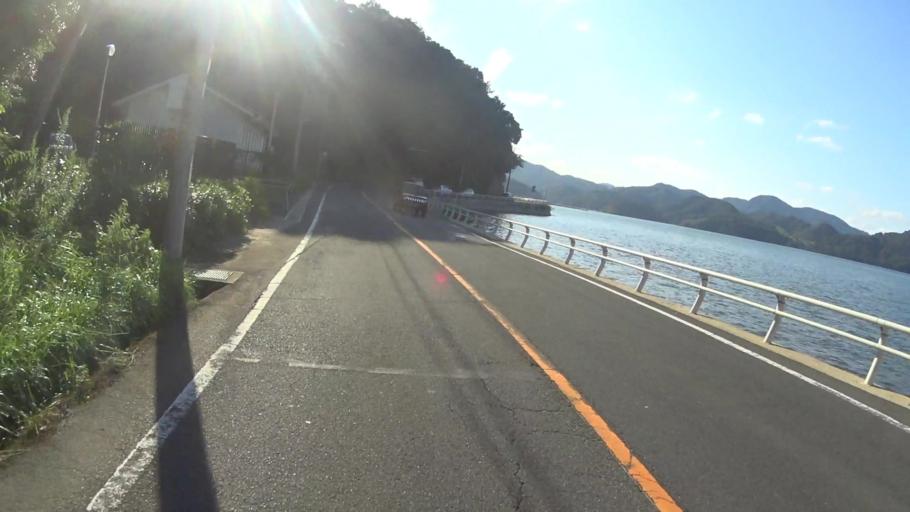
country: JP
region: Hyogo
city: Toyooka
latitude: 35.6061
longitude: 134.9071
